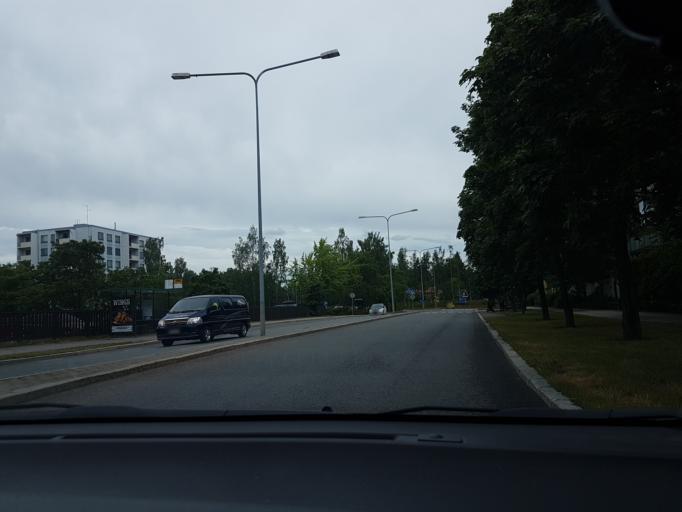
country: FI
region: Uusimaa
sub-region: Helsinki
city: Vantaa
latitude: 60.2763
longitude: 25.0344
